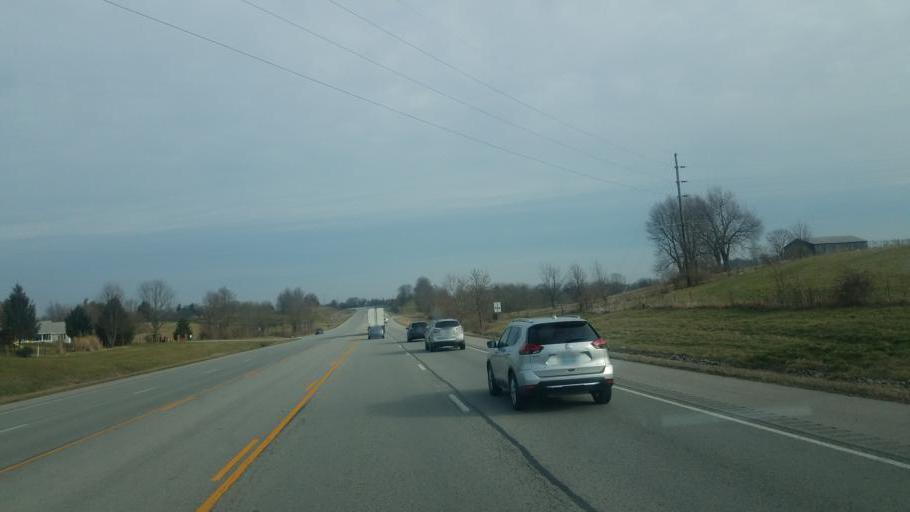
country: US
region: Kentucky
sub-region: Boyle County
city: Junction City
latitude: 37.5918
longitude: -84.7795
